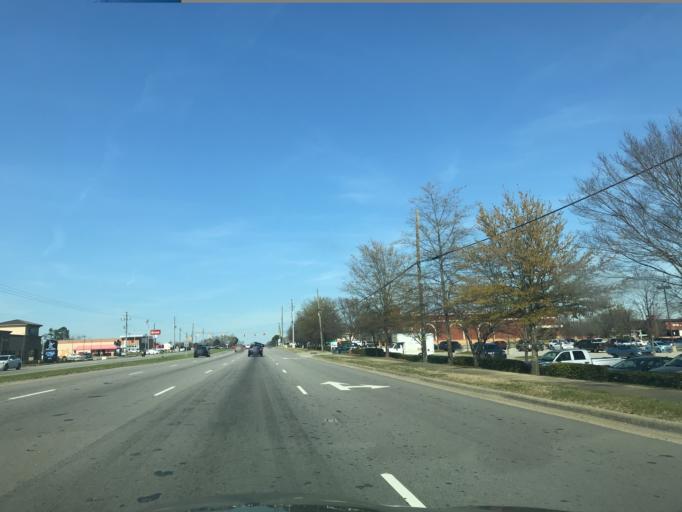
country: US
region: North Carolina
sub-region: Wake County
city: Garner
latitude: 35.6637
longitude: -78.7012
